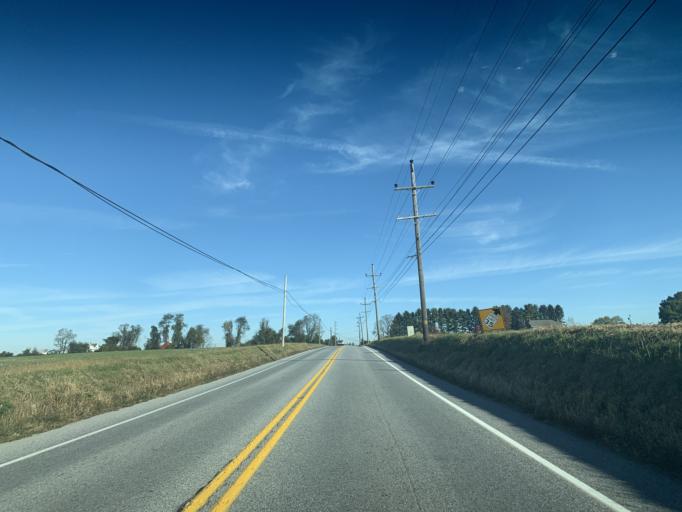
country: US
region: Pennsylvania
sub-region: Chester County
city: Parkesburg
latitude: 39.8806
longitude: -75.9218
